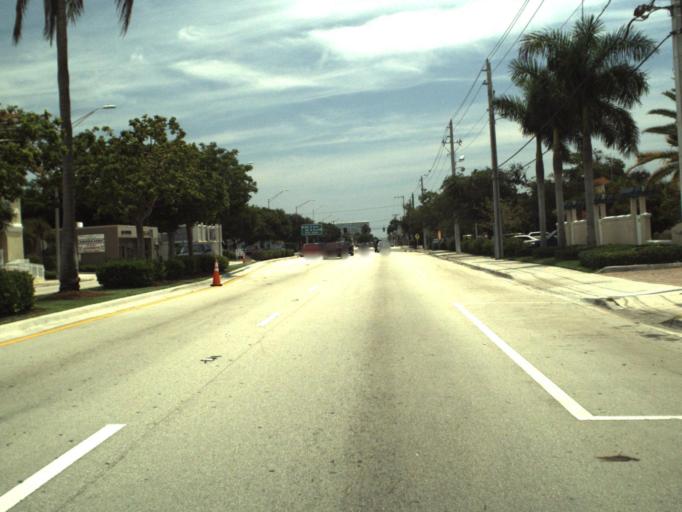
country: US
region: Florida
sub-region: Broward County
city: Pompano Beach
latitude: 26.2316
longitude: -80.1157
